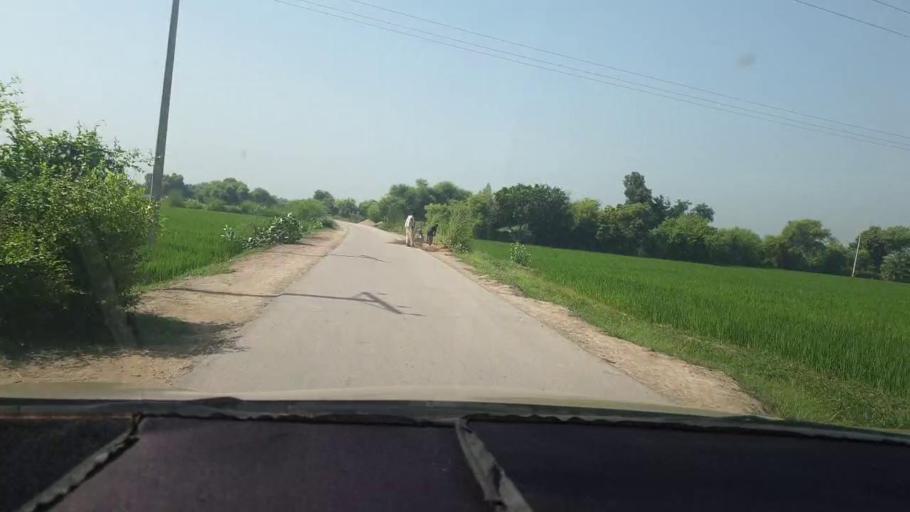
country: PK
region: Sindh
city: Kambar
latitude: 27.5857
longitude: 68.0484
